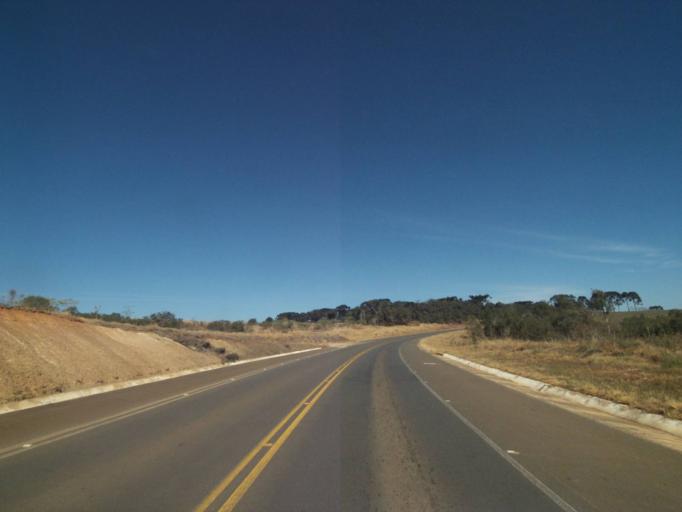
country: BR
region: Parana
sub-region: Tibagi
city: Tibagi
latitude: -24.6931
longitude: -50.4411
